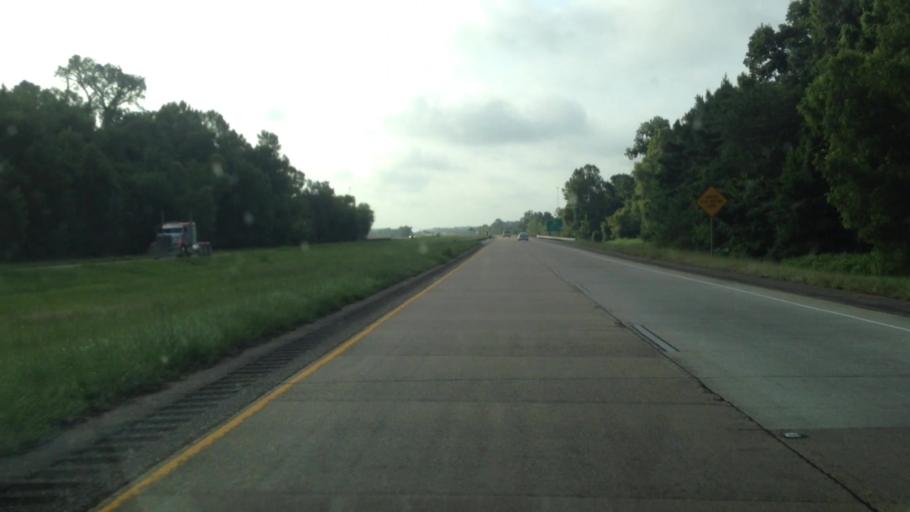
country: US
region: Louisiana
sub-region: Rapides Parish
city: Lecompte
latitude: 31.0211
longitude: -92.3915
